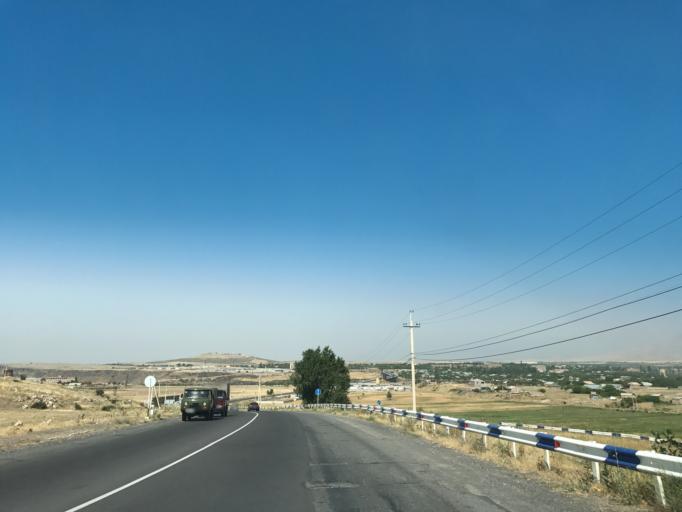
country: AM
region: Kotayk'i Marz
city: Arzni
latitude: 40.2857
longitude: 44.6054
